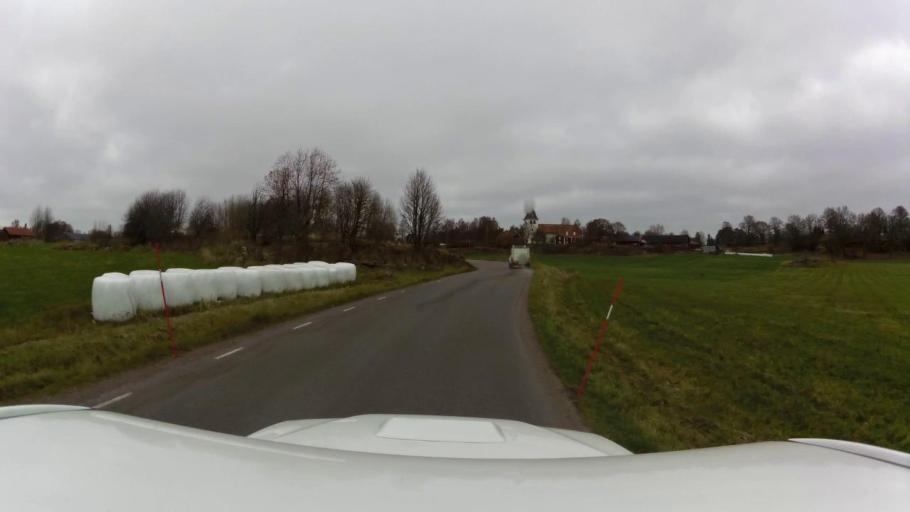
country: SE
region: OEstergoetland
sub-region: Kinda Kommun
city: Rimforsa
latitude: 58.2342
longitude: 15.6907
